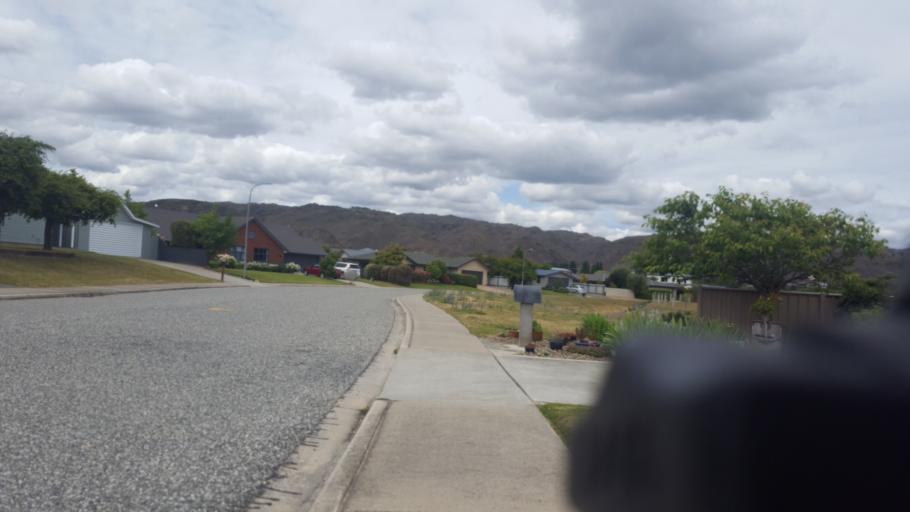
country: NZ
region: Otago
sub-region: Queenstown-Lakes District
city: Wanaka
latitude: -45.2537
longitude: 169.3842
